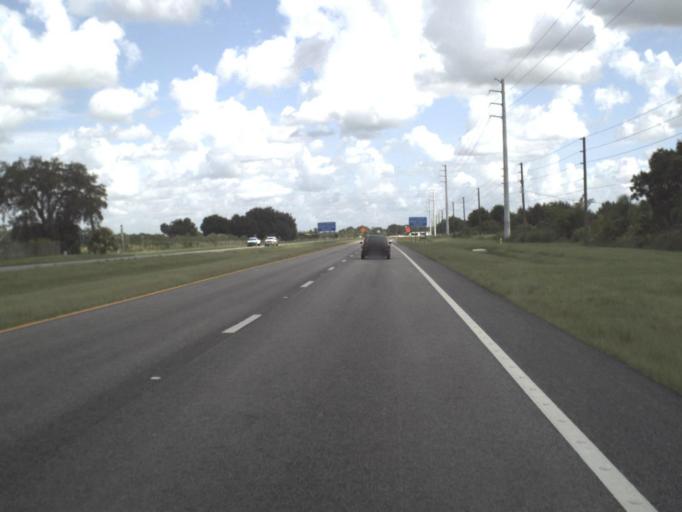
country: US
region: Florida
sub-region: Charlotte County
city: Harbour Heights
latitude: 27.0703
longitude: -81.9581
